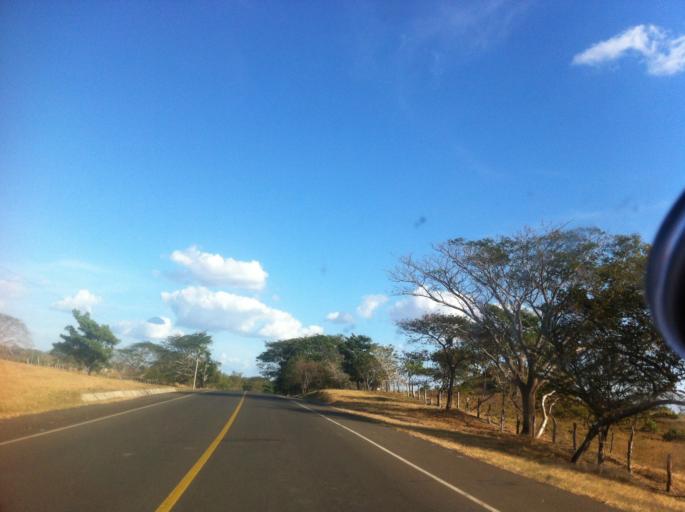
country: NI
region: Chontales
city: Acoyapa
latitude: 11.9278
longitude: -85.1408
